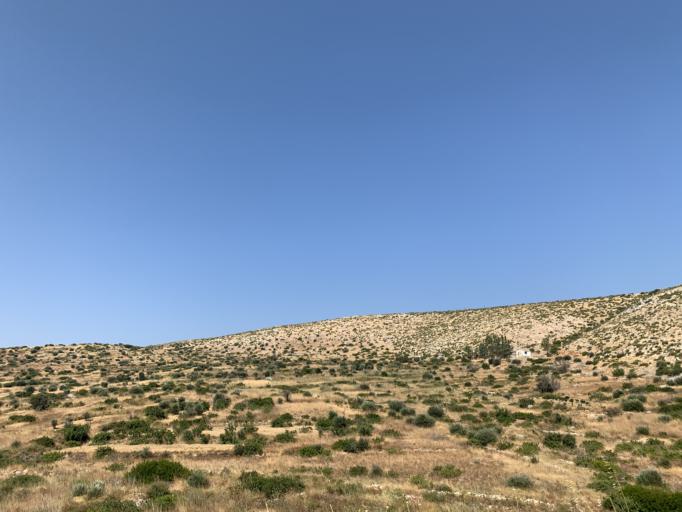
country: GR
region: North Aegean
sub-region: Chios
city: Thymiana
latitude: 38.3119
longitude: 26.0036
